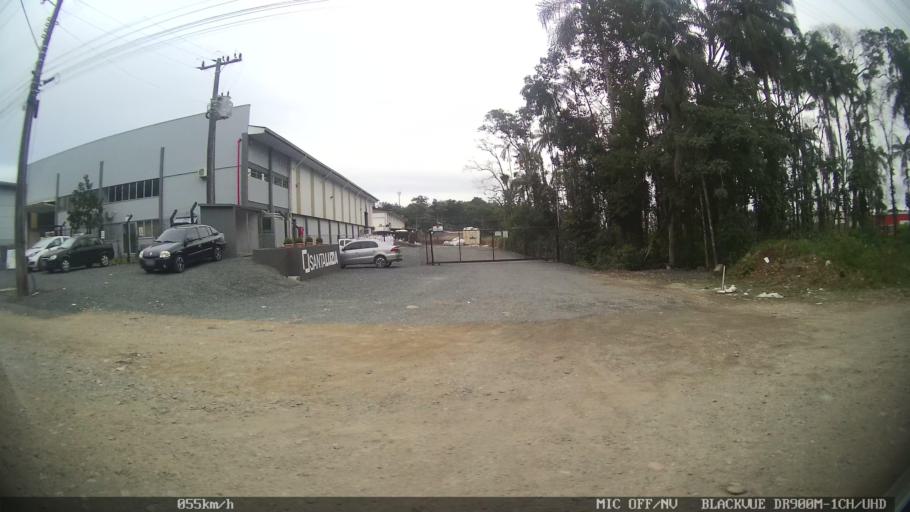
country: BR
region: Santa Catarina
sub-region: Joinville
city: Joinville
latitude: -26.2318
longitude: -48.9031
